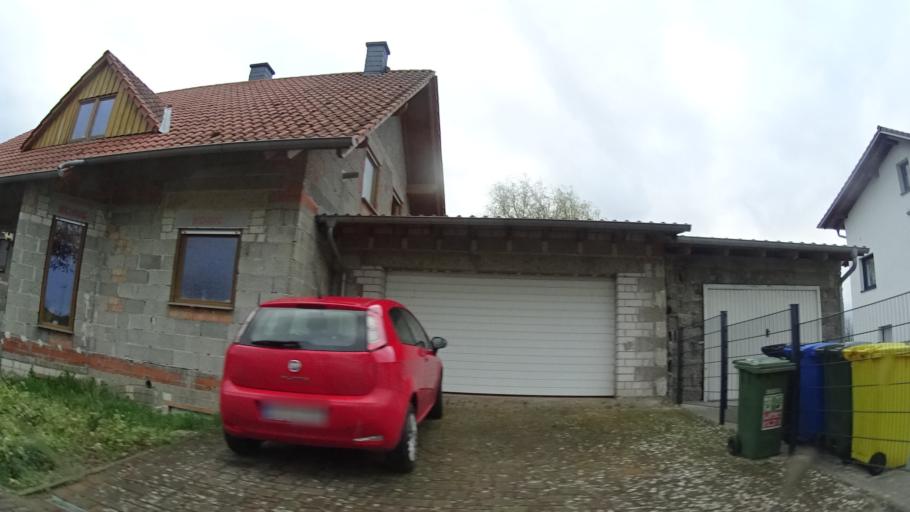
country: DE
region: Rheinland-Pfalz
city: Eppelsheim
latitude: 49.7072
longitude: 8.1624
